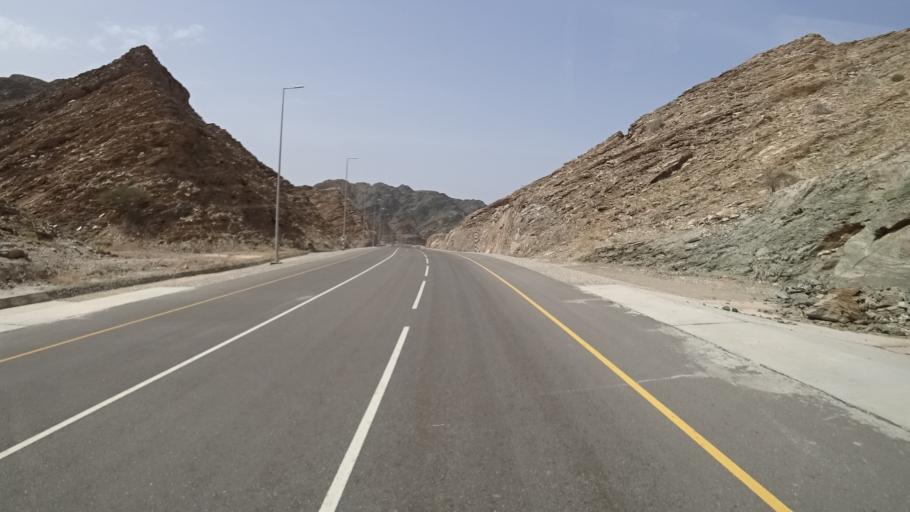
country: OM
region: Muhafazat Masqat
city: Muscat
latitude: 23.4458
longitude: 58.7577
